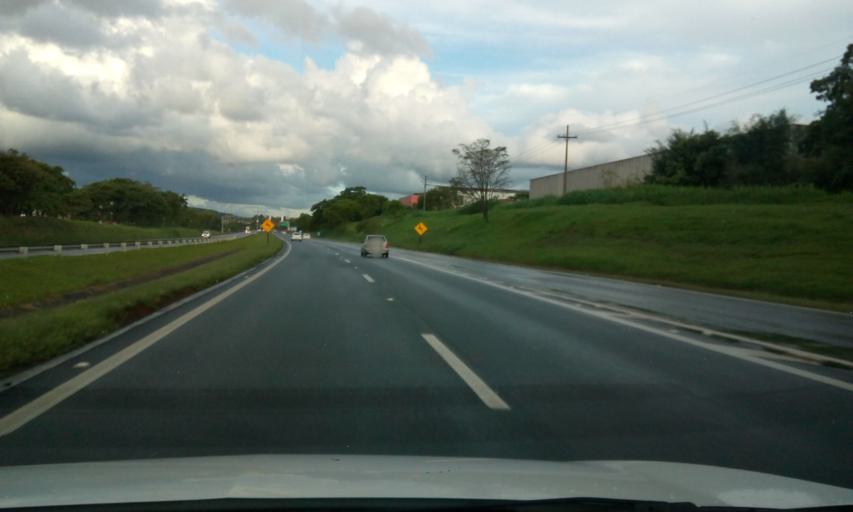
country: BR
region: Sao Paulo
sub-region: Atibaia
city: Atibaia
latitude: -23.1077
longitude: -46.5157
